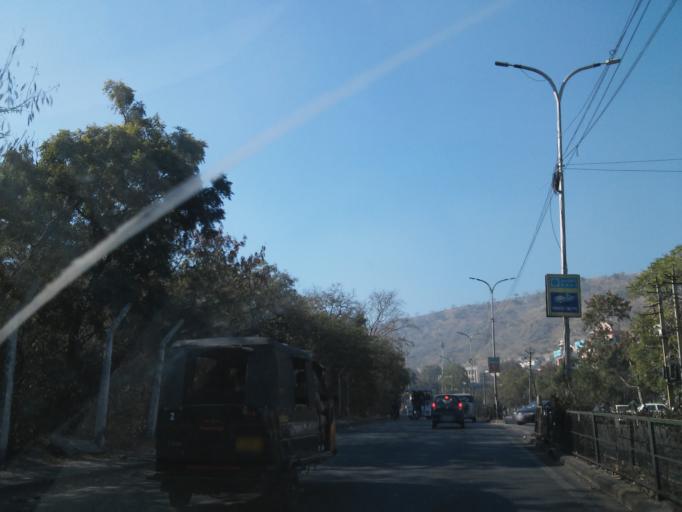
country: IN
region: Rajasthan
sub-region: Udaipur
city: Udaipur
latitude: 24.5666
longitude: 73.6952
